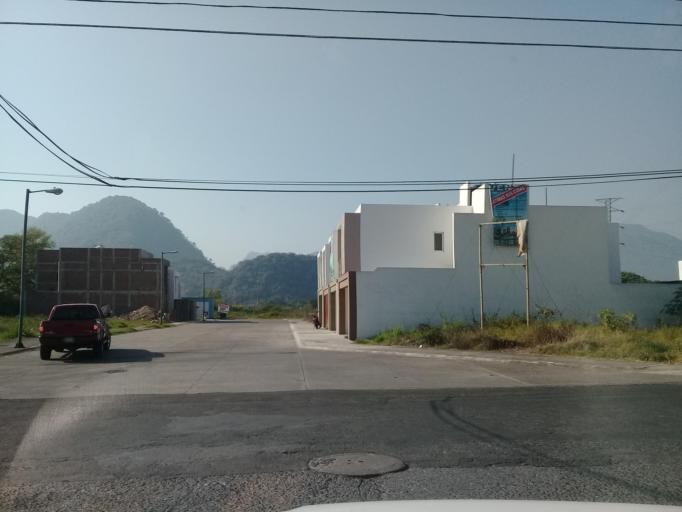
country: MX
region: Veracruz
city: Ixtac Zoquitlan
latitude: 18.8533
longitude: -97.0685
